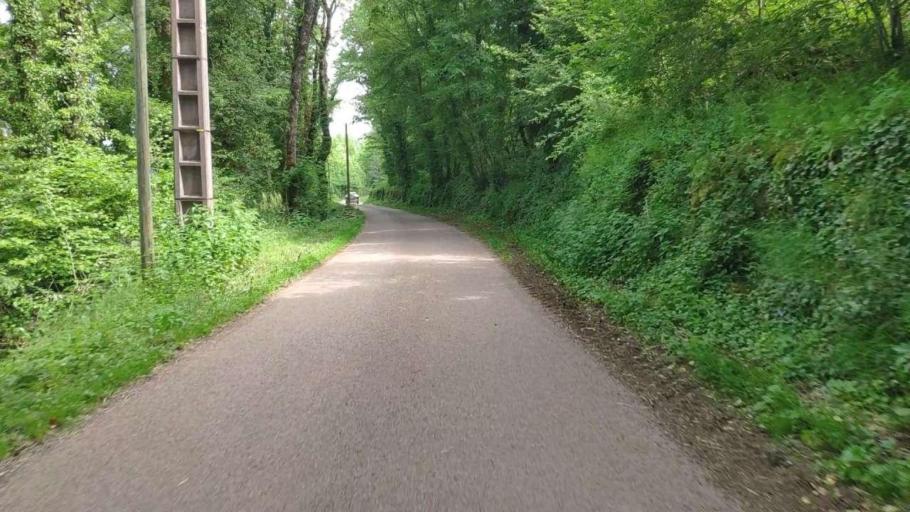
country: FR
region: Franche-Comte
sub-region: Departement du Jura
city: Poligny
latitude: 46.7728
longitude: 5.6282
